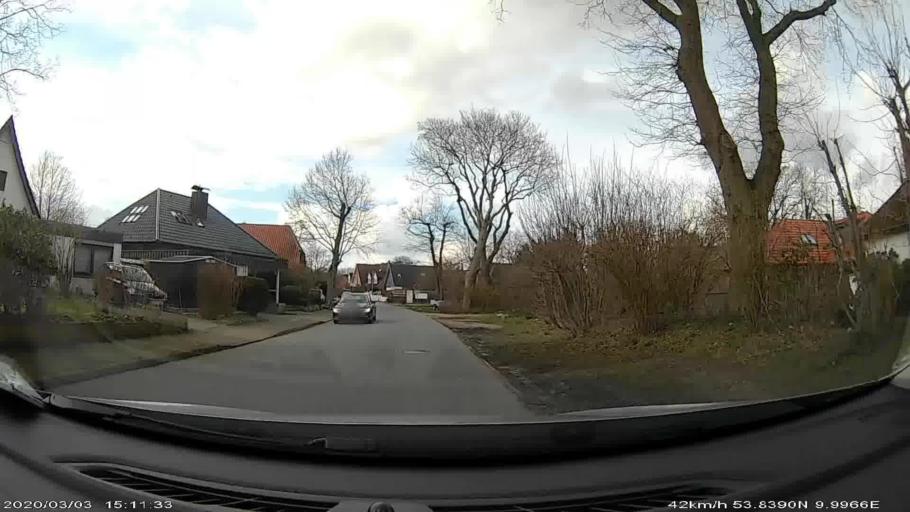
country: DE
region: Schleswig-Holstein
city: Oersdorf
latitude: 53.8389
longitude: 9.9968
